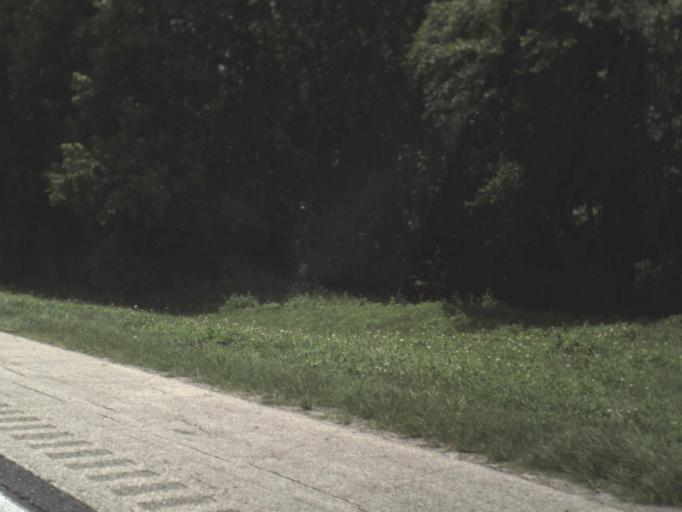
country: US
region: Florida
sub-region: Alachua County
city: Alachua
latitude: 29.6730
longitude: -82.4313
